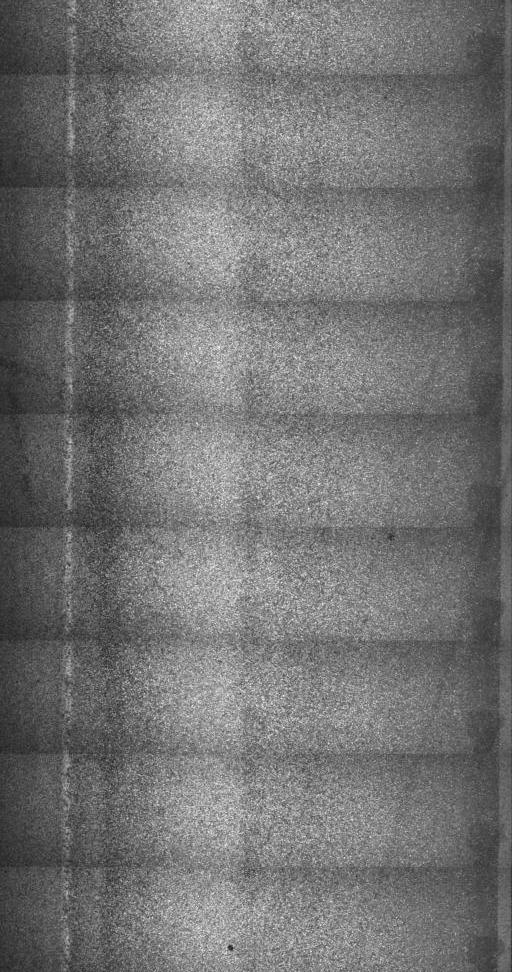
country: US
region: Vermont
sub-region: Chittenden County
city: Colchester
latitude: 44.6363
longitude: -73.2673
